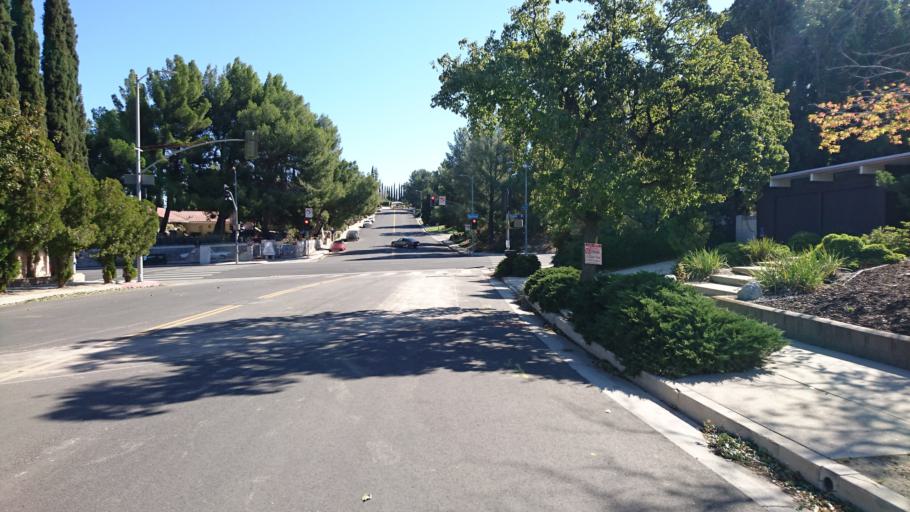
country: US
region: California
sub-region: Los Angeles County
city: San Fernando
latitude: 34.3037
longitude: -118.5016
